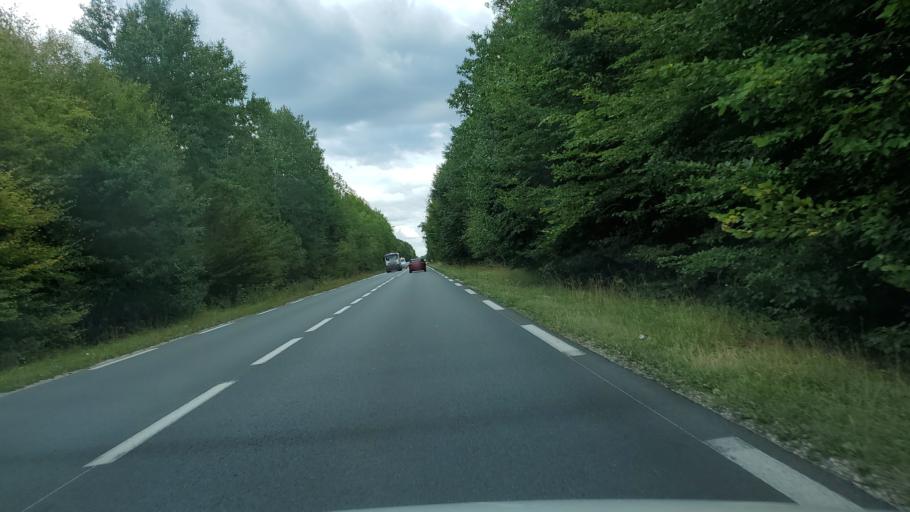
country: FR
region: Ile-de-France
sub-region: Departement de Seine-et-Marne
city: Mortcerf
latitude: 48.7785
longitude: 2.8943
